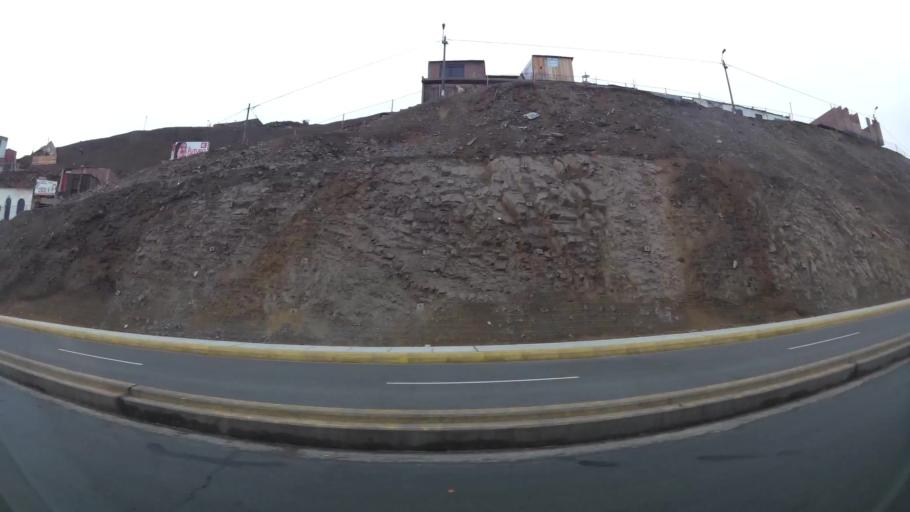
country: PE
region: Lima
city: Ventanilla
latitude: -11.8943
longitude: -77.1265
